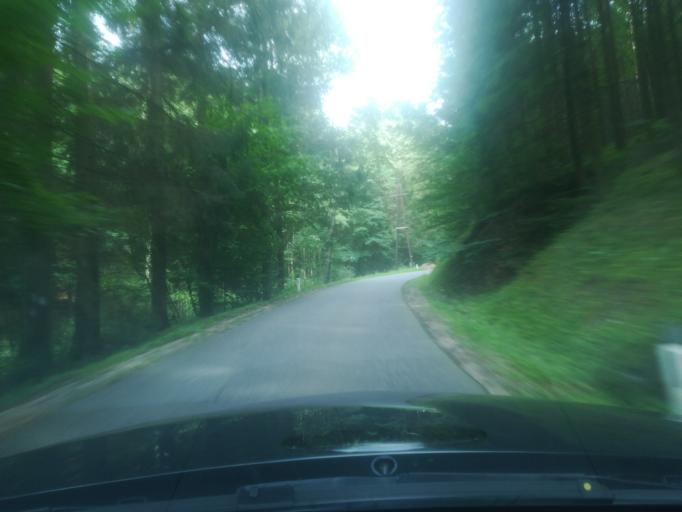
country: AT
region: Upper Austria
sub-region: Politischer Bezirk Perg
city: Perg
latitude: 48.3219
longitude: 14.6598
